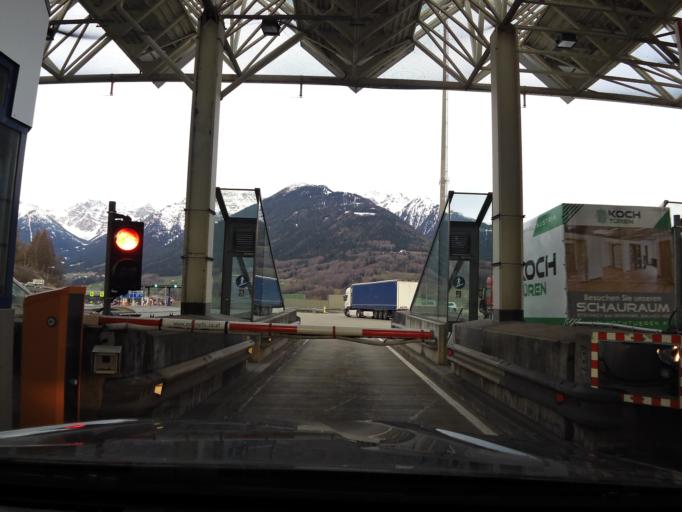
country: AT
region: Tyrol
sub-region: Politischer Bezirk Innsbruck Land
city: Schoenberg im Stubaital
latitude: 47.1853
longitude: 11.4049
